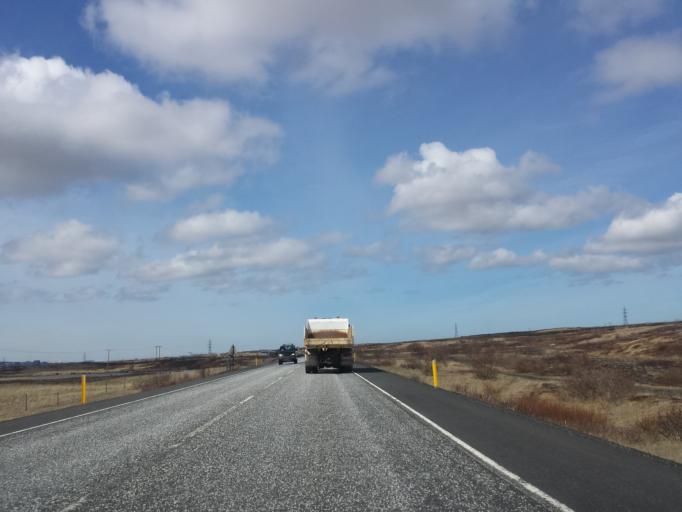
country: IS
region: Capital Region
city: Mosfellsbaer
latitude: 64.0880
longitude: -21.6936
